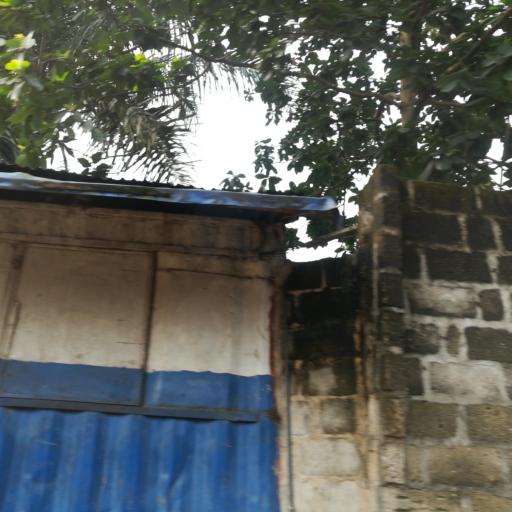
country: NG
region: Rivers
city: Port Harcourt
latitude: 4.8486
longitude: 7.0559
